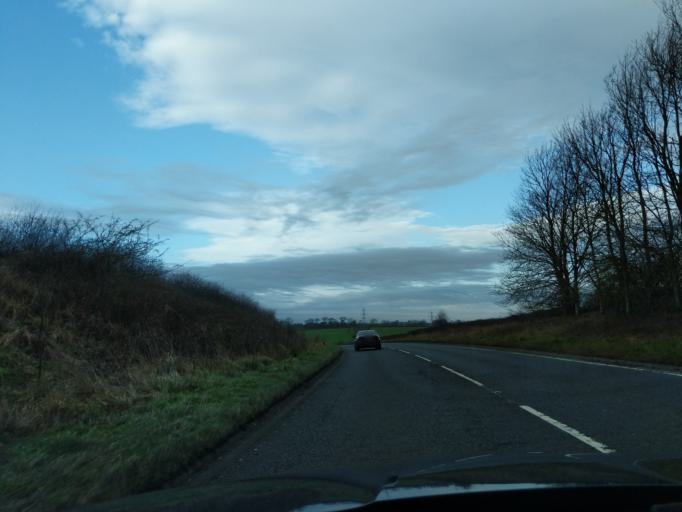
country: GB
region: England
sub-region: Northumberland
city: Meldon
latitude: 55.0966
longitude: -1.8177
